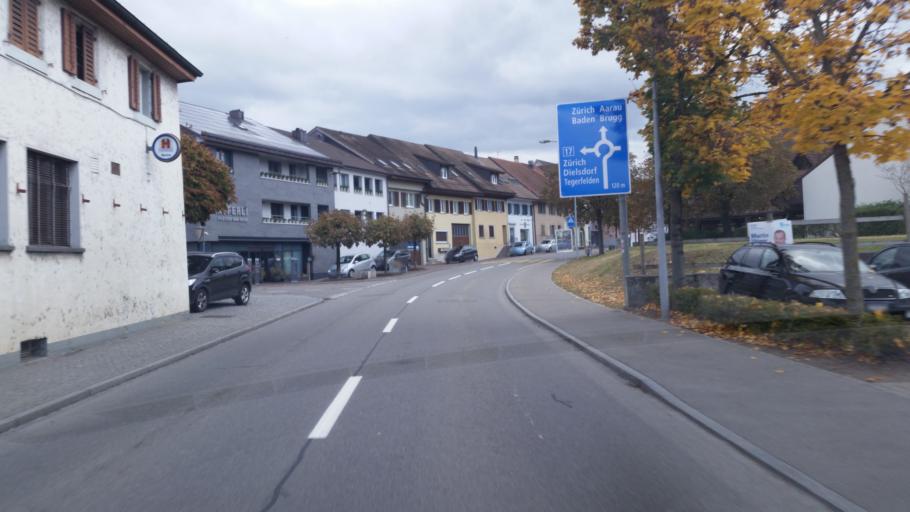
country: CH
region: Aargau
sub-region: Bezirk Zurzach
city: Klingnau
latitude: 47.5724
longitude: 8.2560
